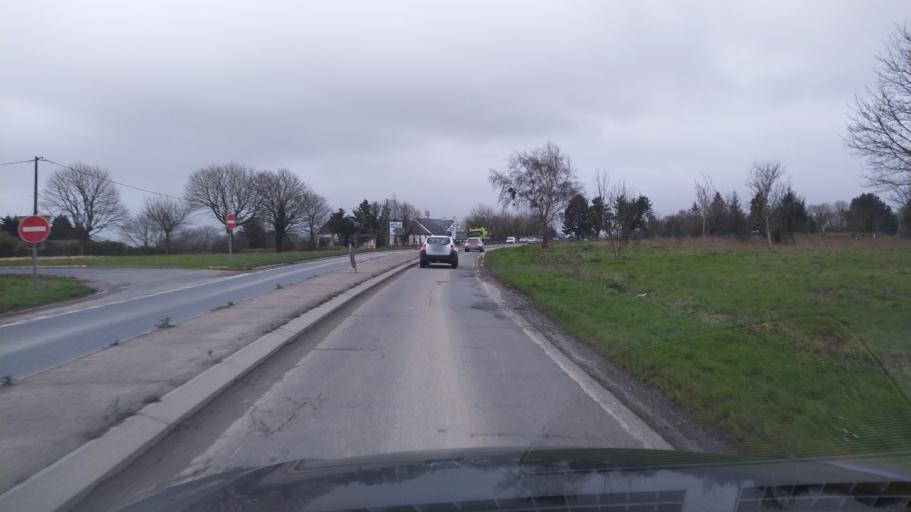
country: FR
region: Brittany
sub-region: Departement du Finistere
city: Landivisiau
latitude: 48.5204
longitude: -4.0572
